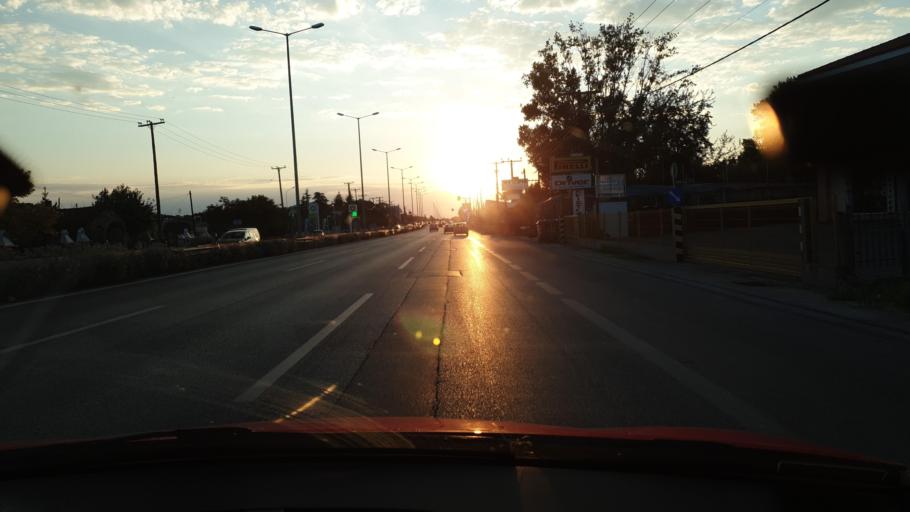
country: GR
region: Central Macedonia
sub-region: Nomos Thessalonikis
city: Plagiari
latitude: 40.5004
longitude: 22.9546
